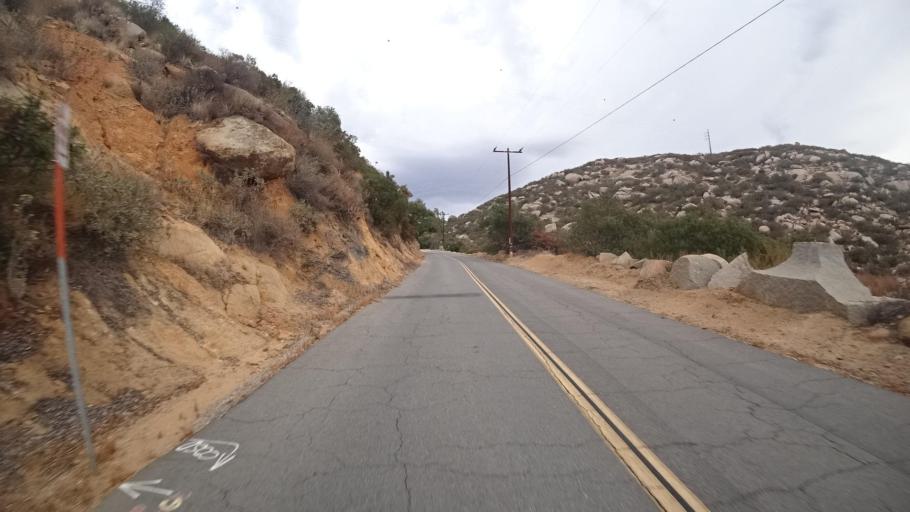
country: US
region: California
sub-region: San Diego County
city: Eucalyptus Hills
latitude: 32.9548
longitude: -116.9151
